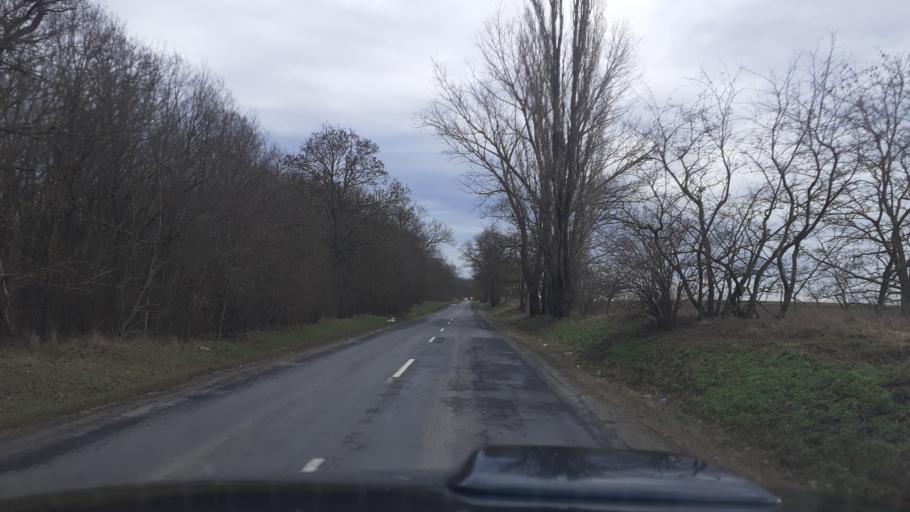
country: HU
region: Fejer
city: Sarosd
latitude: 47.0275
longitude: 18.6683
